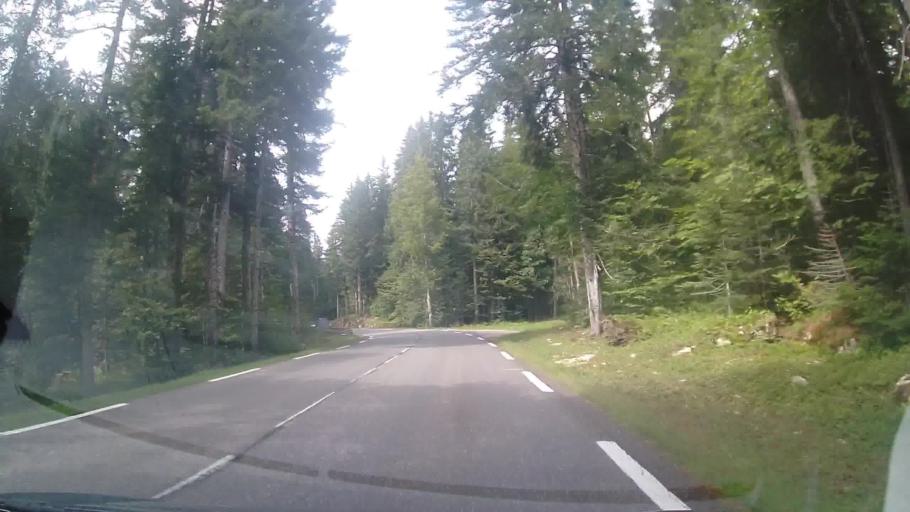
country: FR
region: Rhone-Alpes
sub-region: Departement de l'Ain
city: Gex
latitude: 46.3937
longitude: 6.0492
